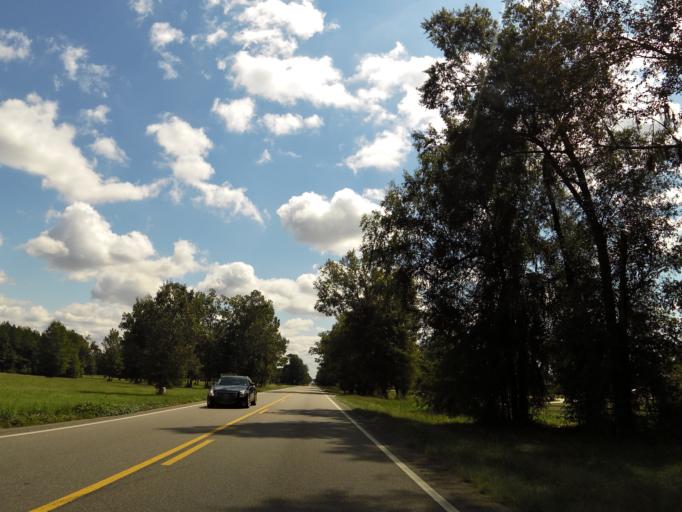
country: US
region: Alabama
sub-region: Dallas County
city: Selma
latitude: 32.4643
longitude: -87.0924
